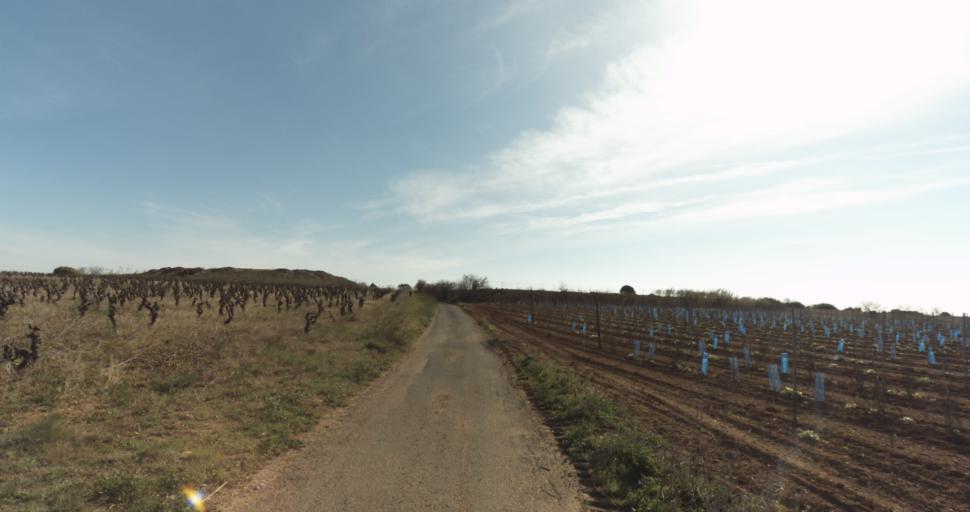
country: FR
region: Languedoc-Roussillon
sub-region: Departement de l'Herault
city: Marseillan
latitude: 43.3526
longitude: 3.5040
